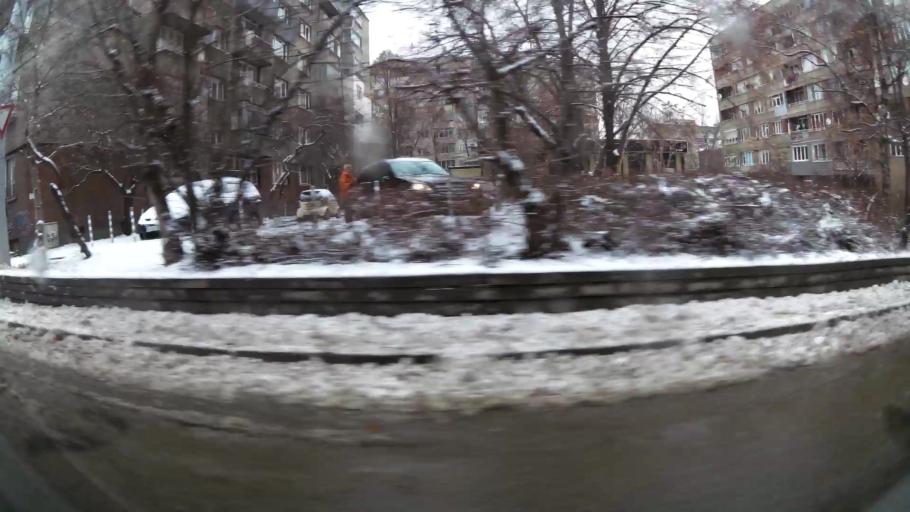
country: BG
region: Sofia-Capital
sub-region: Stolichna Obshtina
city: Sofia
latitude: 42.6950
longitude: 23.3549
